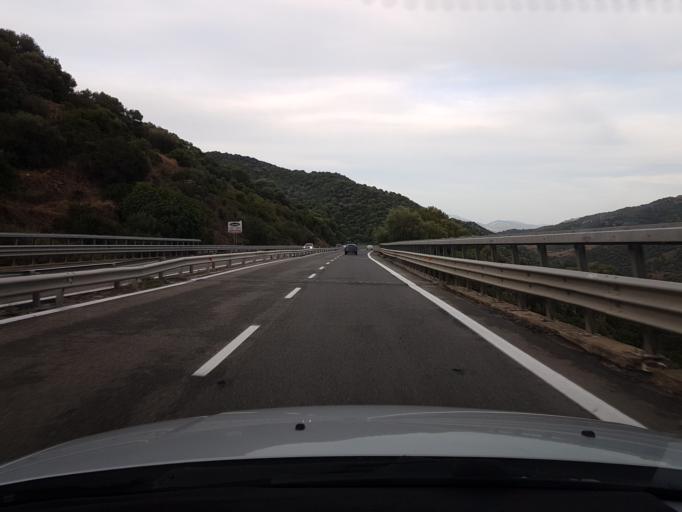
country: IT
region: Sardinia
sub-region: Provincia di Nuoro
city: Nuoro
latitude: 40.3412
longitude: 9.3115
